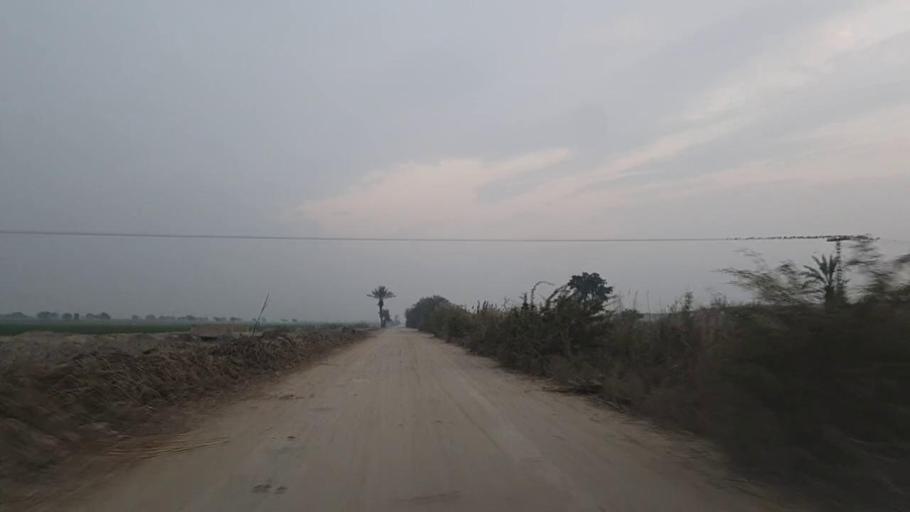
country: PK
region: Sindh
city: Jam Sahib
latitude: 26.3335
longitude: 68.5409
